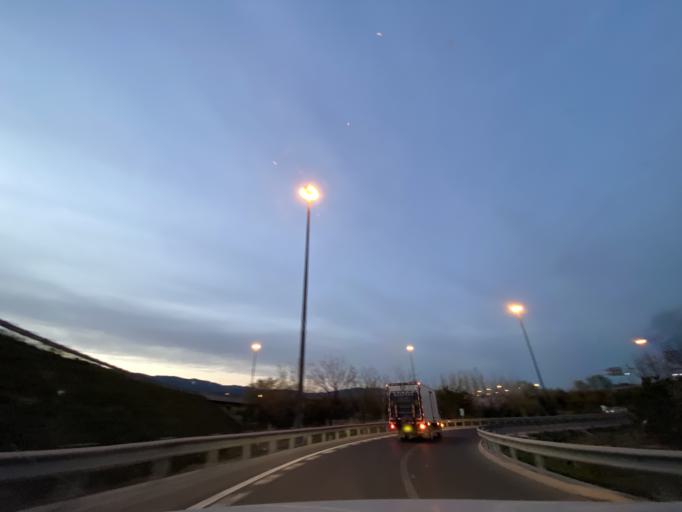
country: CN
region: Beijing
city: Xiangshan
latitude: 39.9535
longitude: 116.2089
